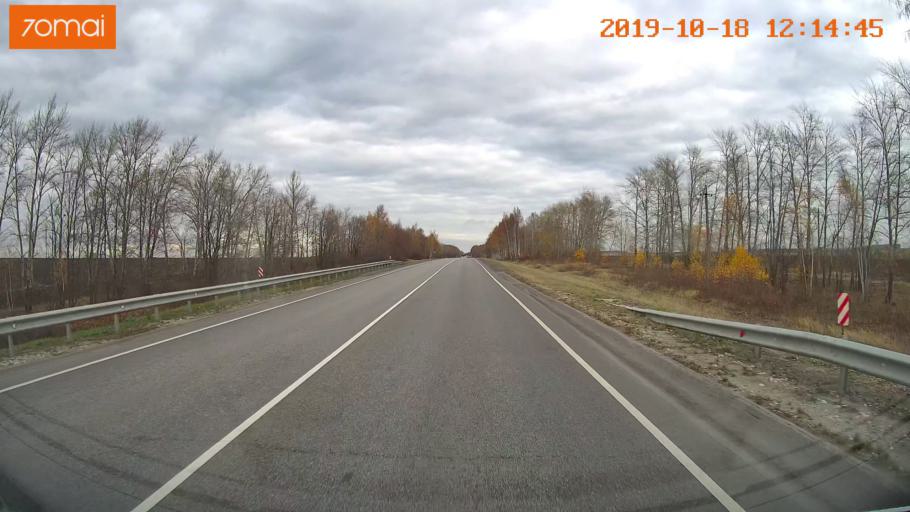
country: RU
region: Rjazan
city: Zakharovo
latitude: 54.4348
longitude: 39.3887
